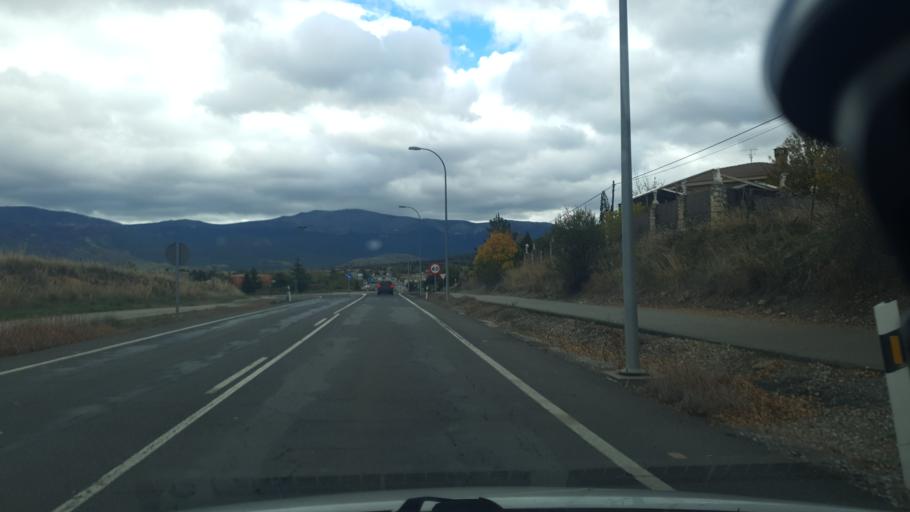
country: ES
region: Castille and Leon
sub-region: Provincia de Segovia
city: Palazuelos de Eresma
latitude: 40.9168
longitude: -4.0699
